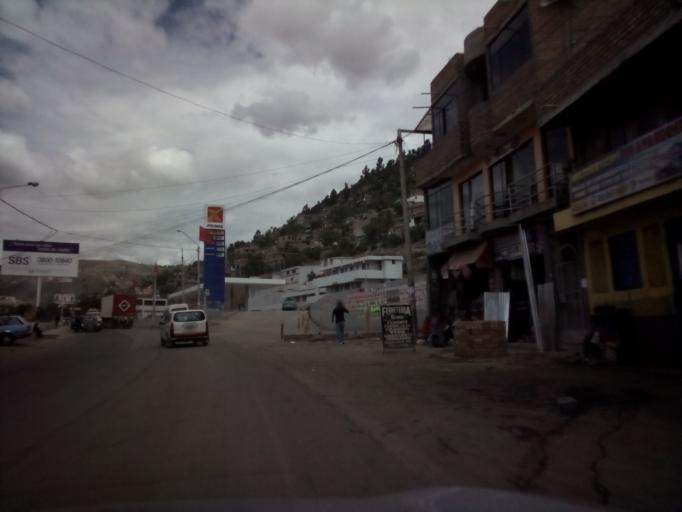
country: PE
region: Ayacucho
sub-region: Provincia de Huamanga
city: Ayacucho
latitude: -13.1468
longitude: -74.2344
